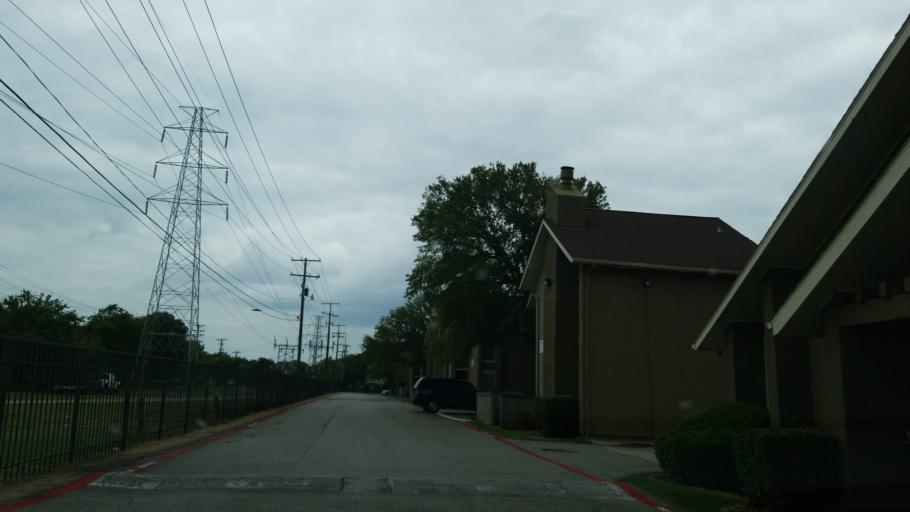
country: US
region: Texas
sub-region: Dallas County
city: Richardson
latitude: 32.9477
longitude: -96.7711
